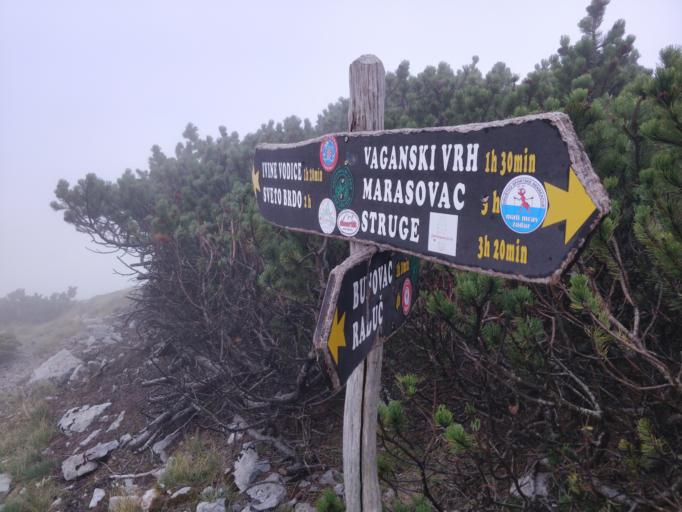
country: HR
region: Zadarska
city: Starigrad
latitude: 44.3548
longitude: 15.5248
